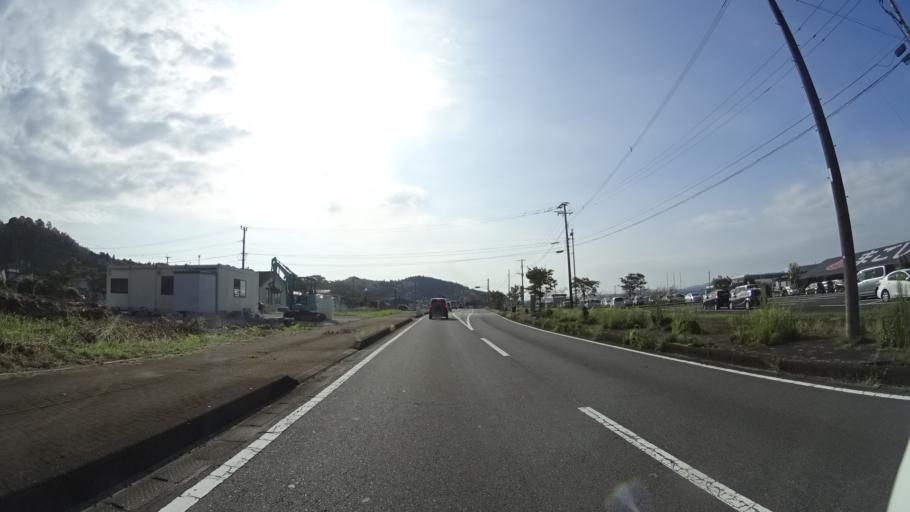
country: JP
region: Kagoshima
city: Okuchi-shinohara
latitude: 32.0134
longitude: 130.6380
